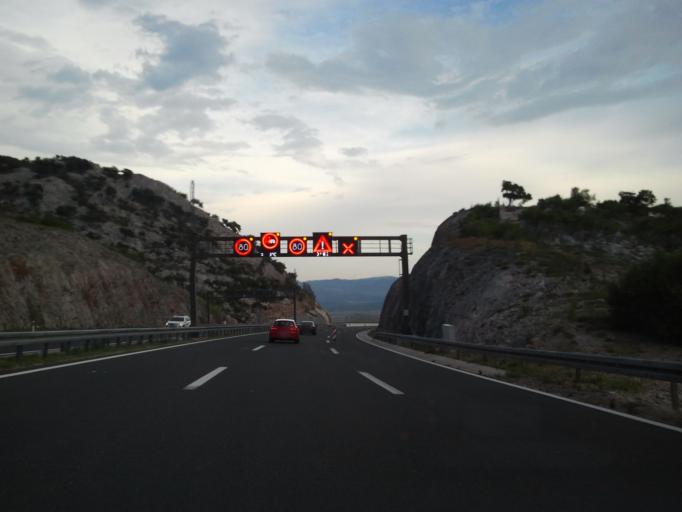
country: HR
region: Zadarska
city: Krusevo
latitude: 44.2538
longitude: 15.6010
